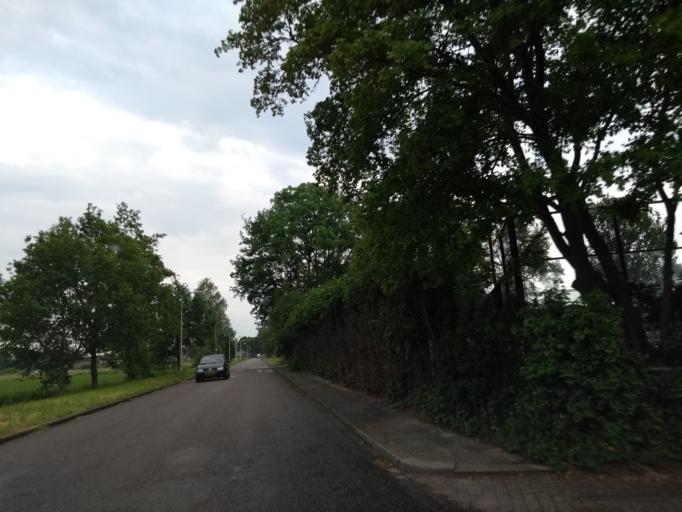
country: NL
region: Overijssel
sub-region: Gemeente Almelo
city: Almelo
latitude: 52.3856
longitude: 6.6713
